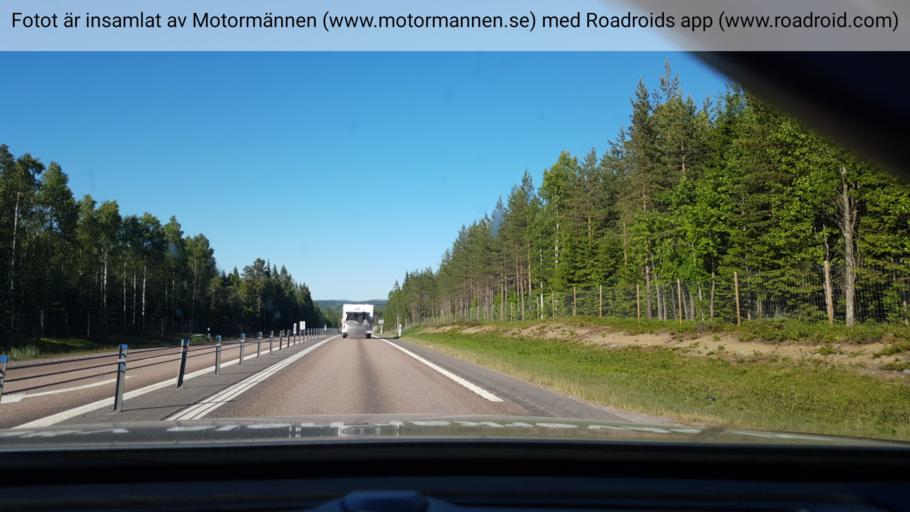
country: SE
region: Vaesternorrland
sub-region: Haernoesands Kommun
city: Haernoesand
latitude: 62.5702
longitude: 17.7413
